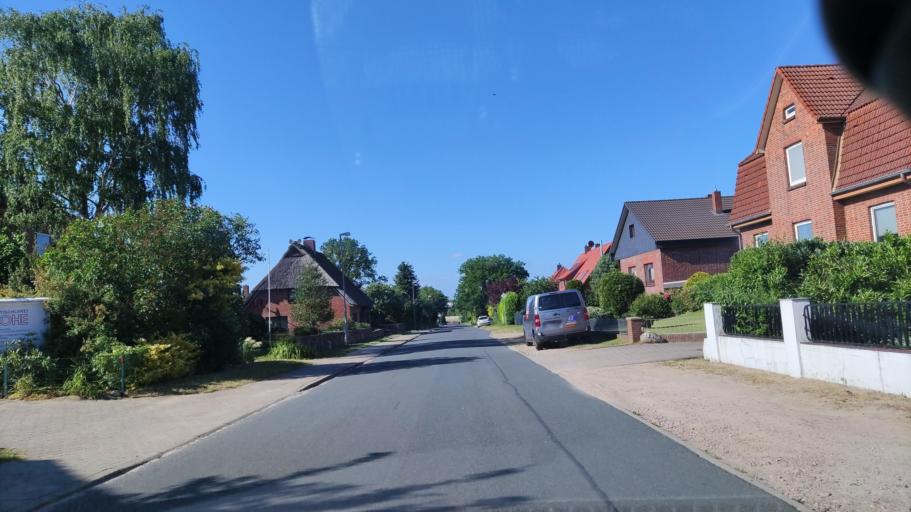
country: DE
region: Lower Saxony
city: Stelle
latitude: 53.3884
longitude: 10.0980
